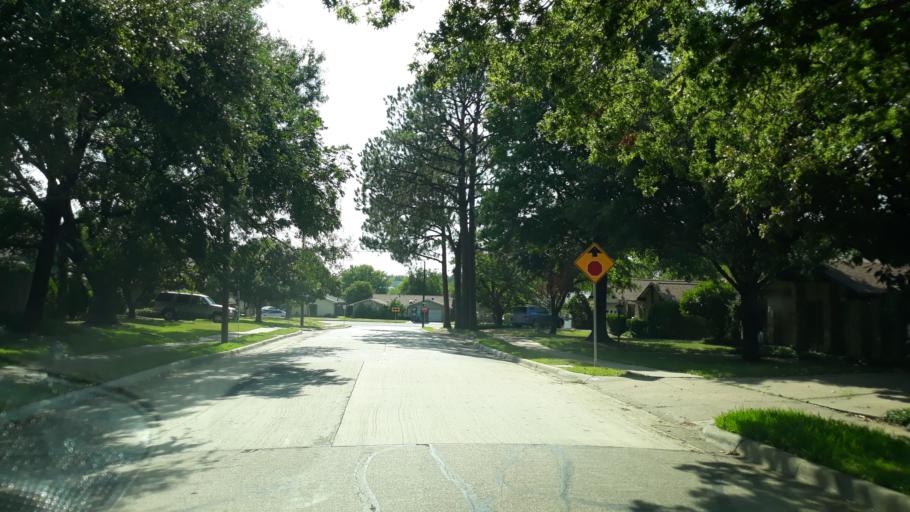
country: US
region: Texas
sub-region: Dallas County
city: Irving
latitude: 32.8435
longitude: -96.9974
